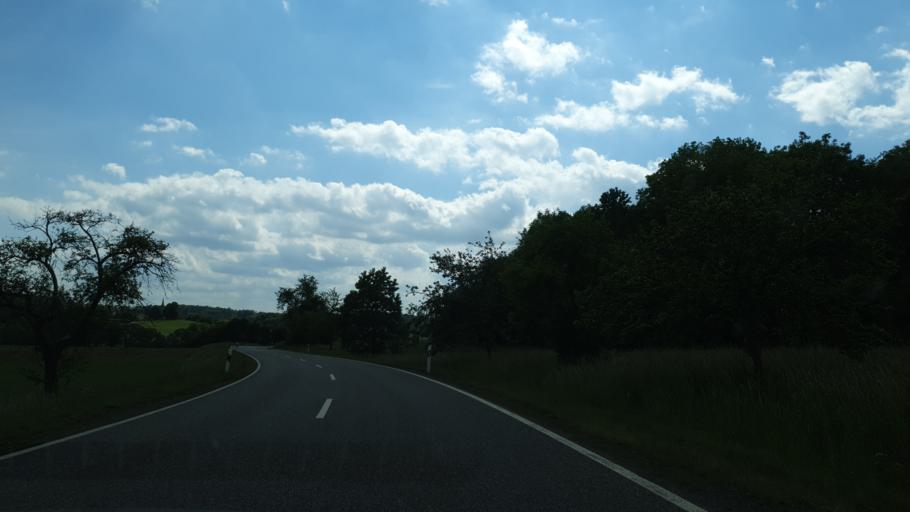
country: DE
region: Rheinland-Pfalz
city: Helferskirchen
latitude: 50.5229
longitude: 7.8209
